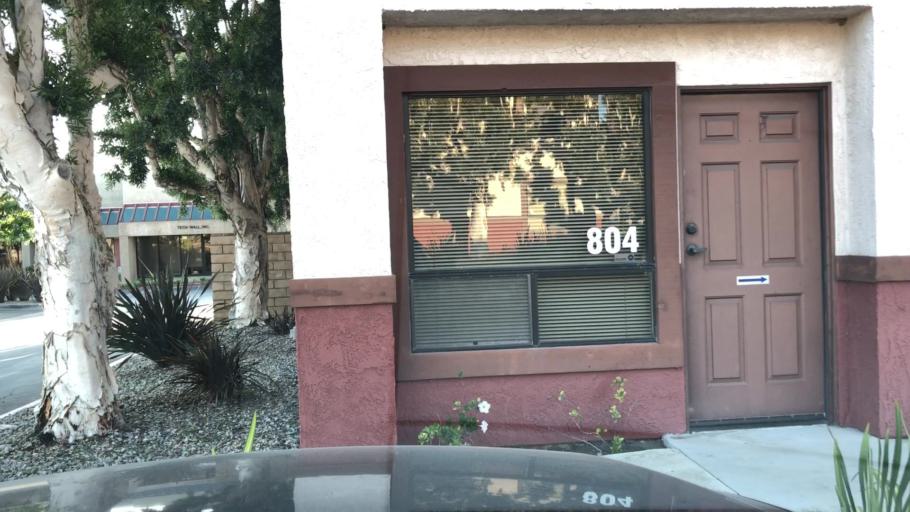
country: US
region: California
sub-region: Ventura County
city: Ventura
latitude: 34.2565
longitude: -119.2332
